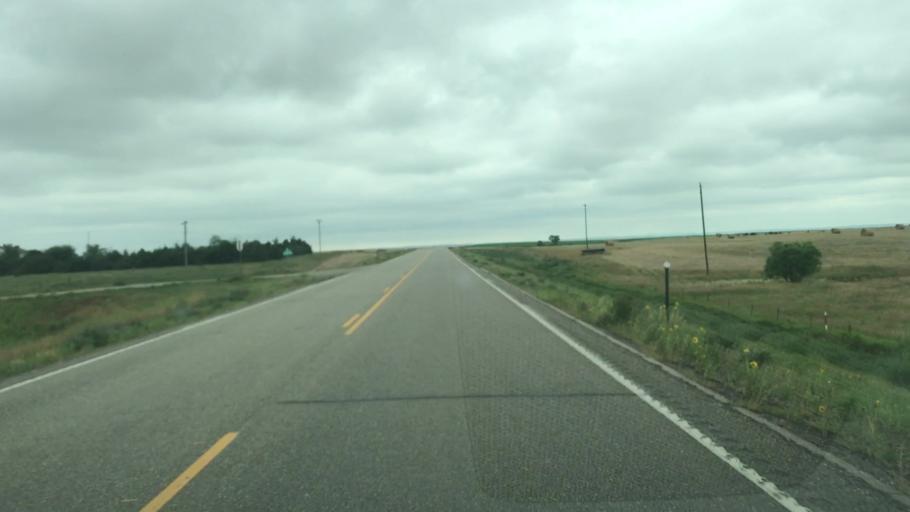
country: US
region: South Dakota
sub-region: Jackson County
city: Kadoka
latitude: 43.8219
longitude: -101.5224
